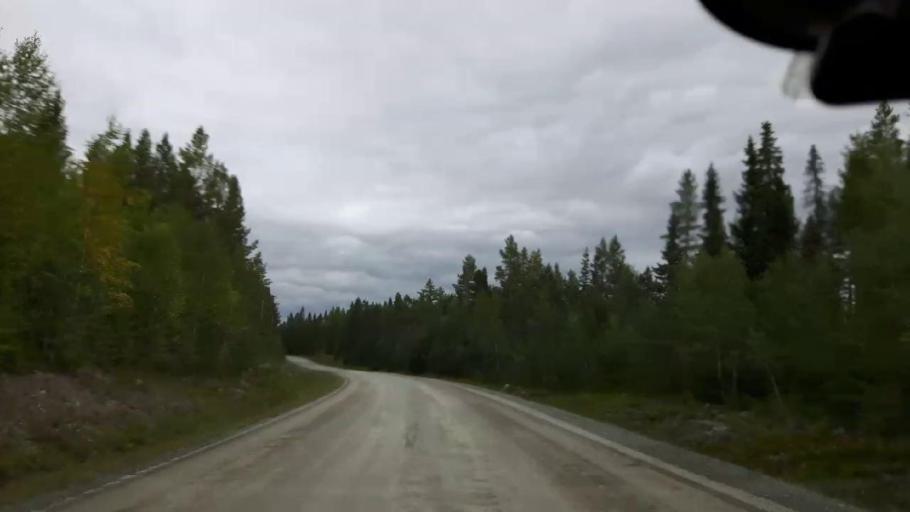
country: SE
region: Jaemtland
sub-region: OEstersunds Kommun
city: Brunflo
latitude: 63.1008
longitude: 15.0586
